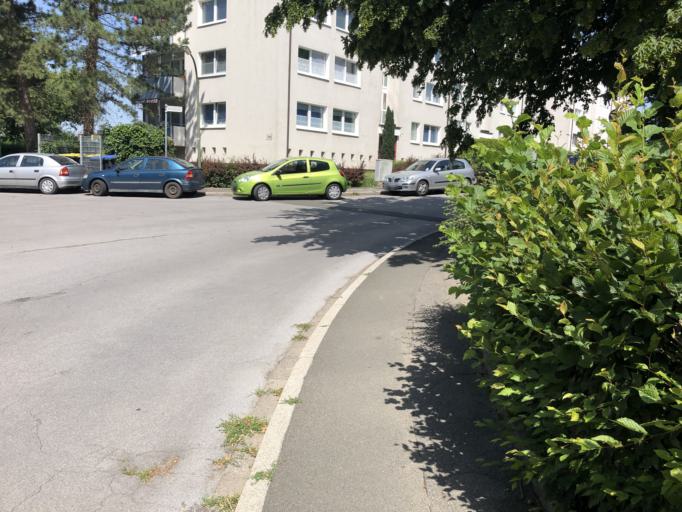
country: DE
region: North Rhine-Westphalia
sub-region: Regierungsbezirk Arnsberg
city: Frondenberg
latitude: 51.4817
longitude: 7.7222
